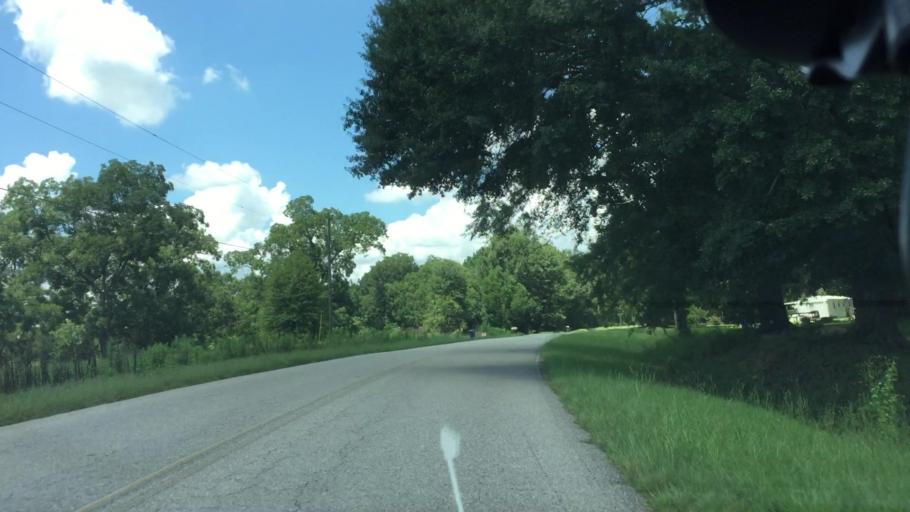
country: US
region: Alabama
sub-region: Pike County
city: Troy
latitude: 31.7519
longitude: -85.9841
